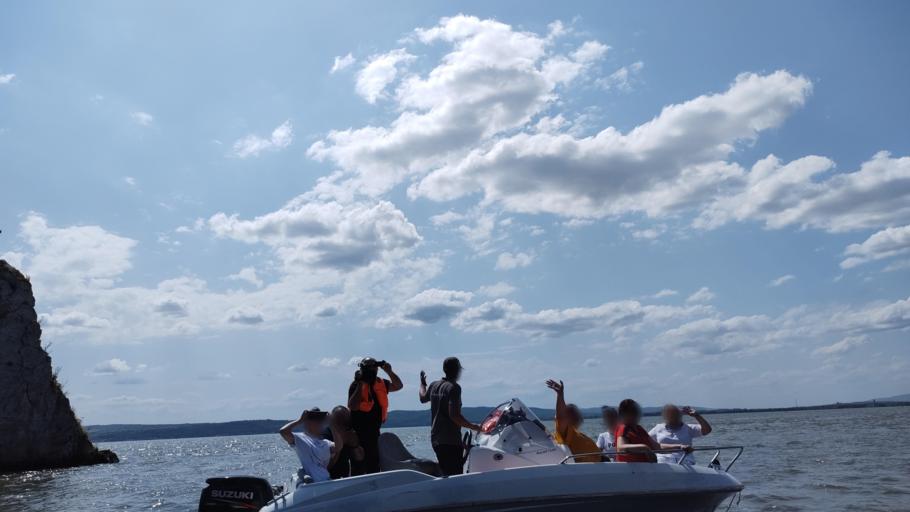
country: RO
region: Caras-Severin
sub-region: Comuna Pescari
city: Coronini
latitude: 44.6734
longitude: 21.6776
